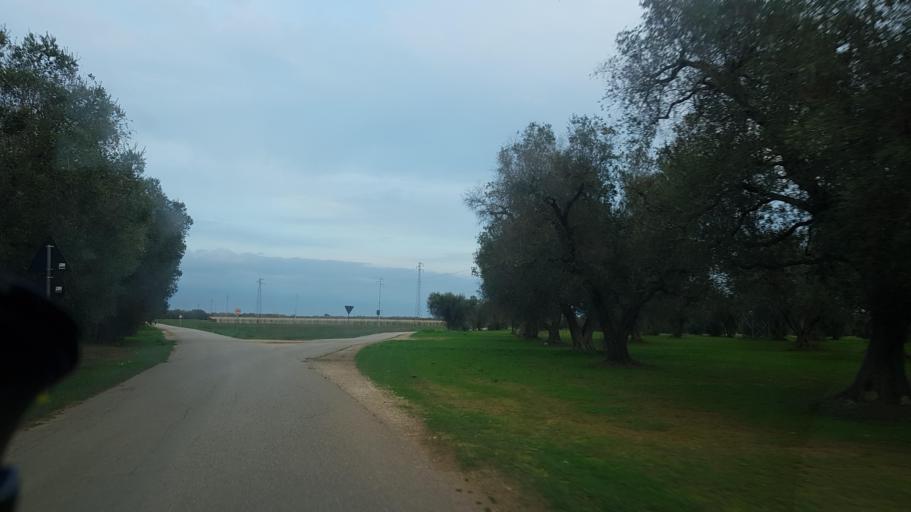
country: IT
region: Apulia
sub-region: Provincia di Brindisi
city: Mesagne
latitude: 40.5363
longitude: 17.7681
